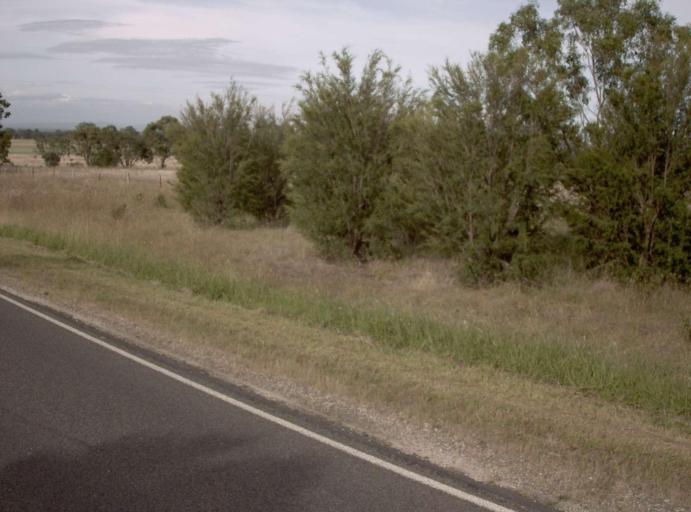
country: AU
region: Victoria
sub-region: Wellington
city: Heyfield
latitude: -38.0237
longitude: 146.6693
